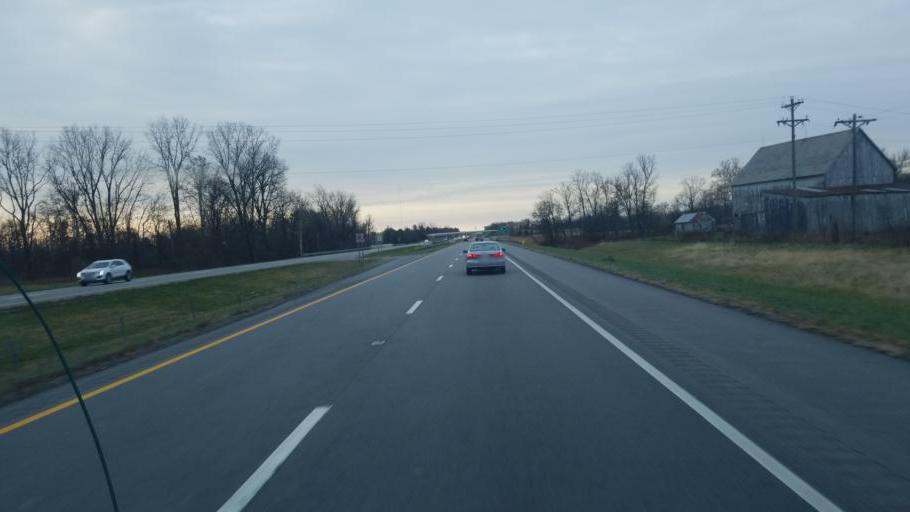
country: US
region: Ohio
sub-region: Auglaize County
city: Wapakoneta
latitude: 40.5924
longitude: -84.1617
